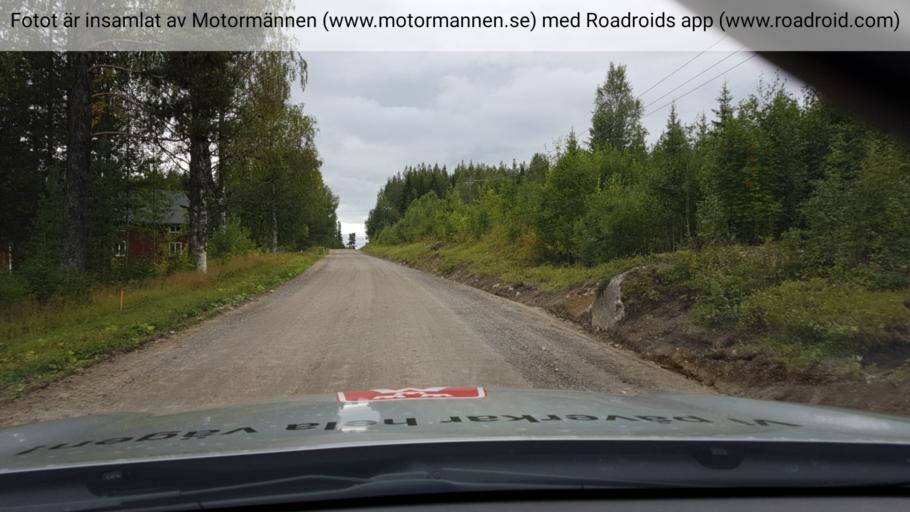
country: SE
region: Jaemtland
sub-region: Ragunda Kommun
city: Hammarstrand
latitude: 62.9123
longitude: 16.0965
